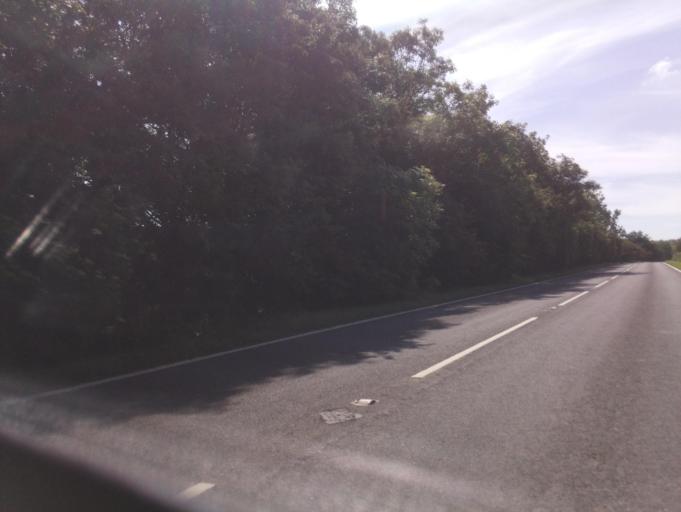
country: GB
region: England
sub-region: North Lincolnshire
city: Manton
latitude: 53.5046
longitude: -0.5822
